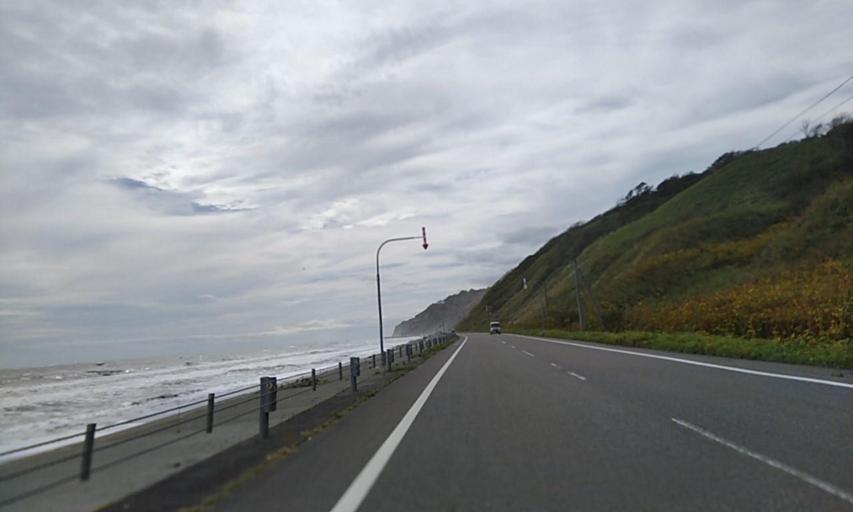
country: JP
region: Hokkaido
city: Obihiro
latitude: 42.7802
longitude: 143.7833
